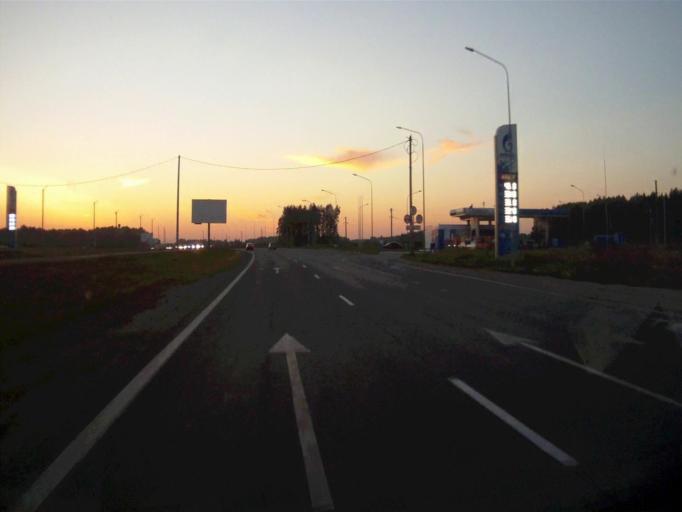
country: RU
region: Chelyabinsk
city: Roshchino
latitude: 55.1877
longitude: 61.2373
